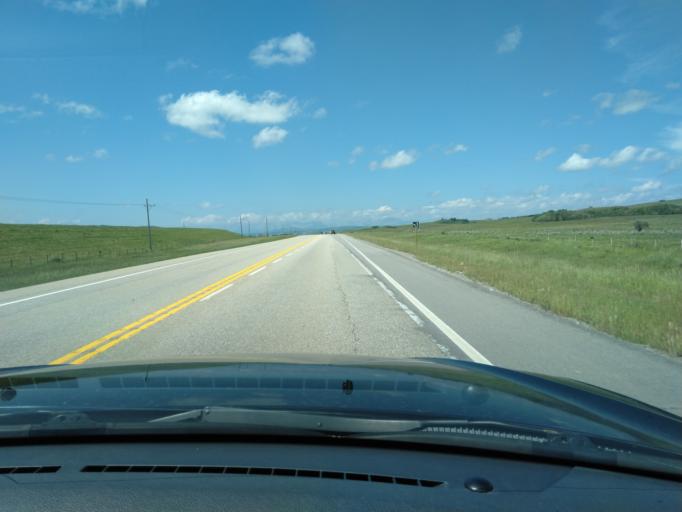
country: CA
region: Alberta
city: Cochrane
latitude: 51.2261
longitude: -114.5920
